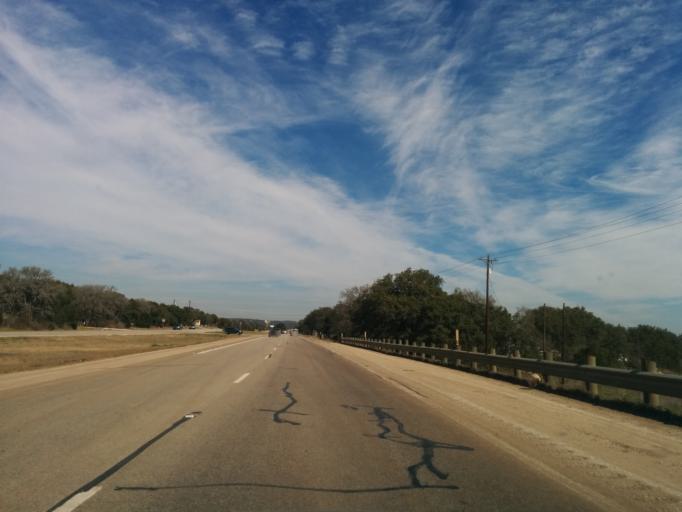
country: US
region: Texas
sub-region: Comal County
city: Bulverde
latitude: 29.8376
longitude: -98.4108
